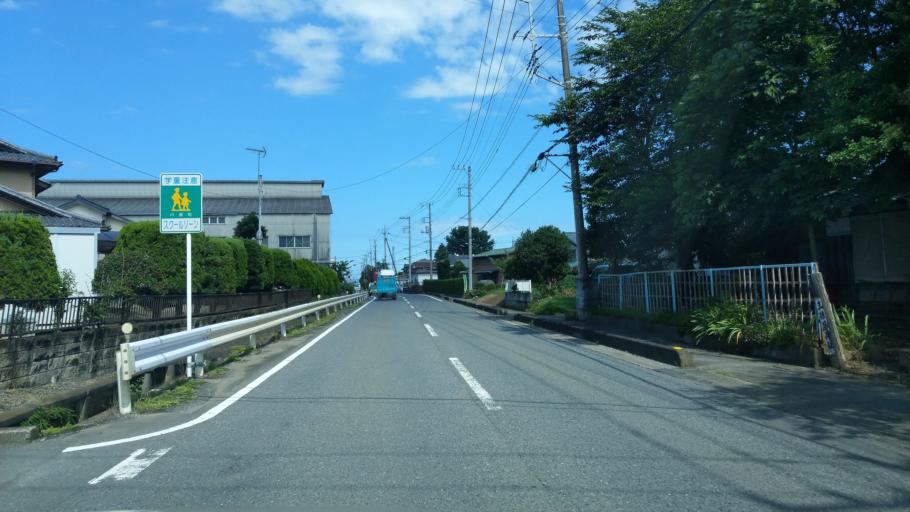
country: JP
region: Saitama
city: Okegawa
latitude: 35.9770
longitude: 139.4930
